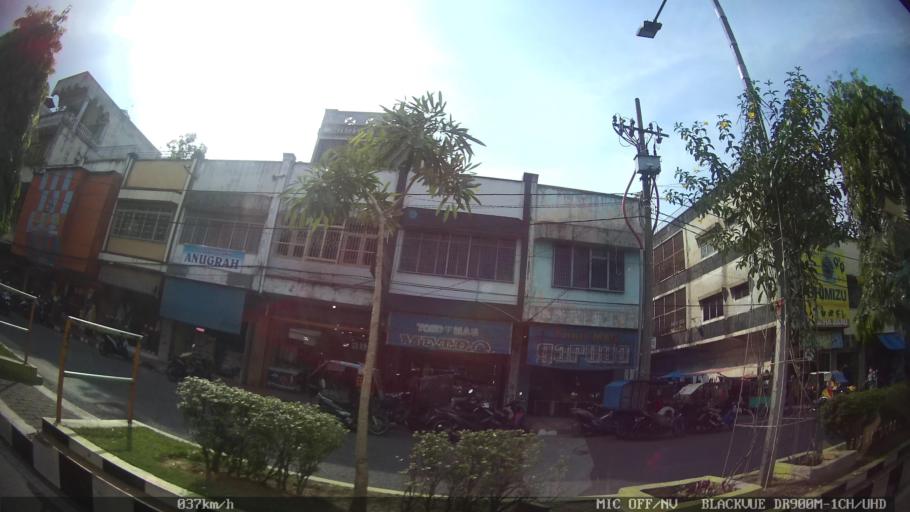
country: ID
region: North Sumatra
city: Binjai
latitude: 3.6087
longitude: 98.4900
